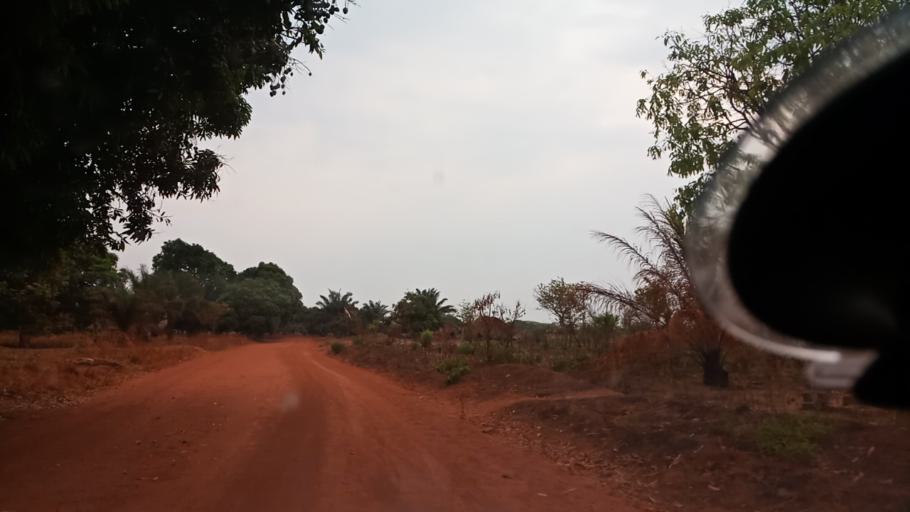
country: ZM
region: Luapula
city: Nchelenge
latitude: -9.1598
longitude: 28.2830
